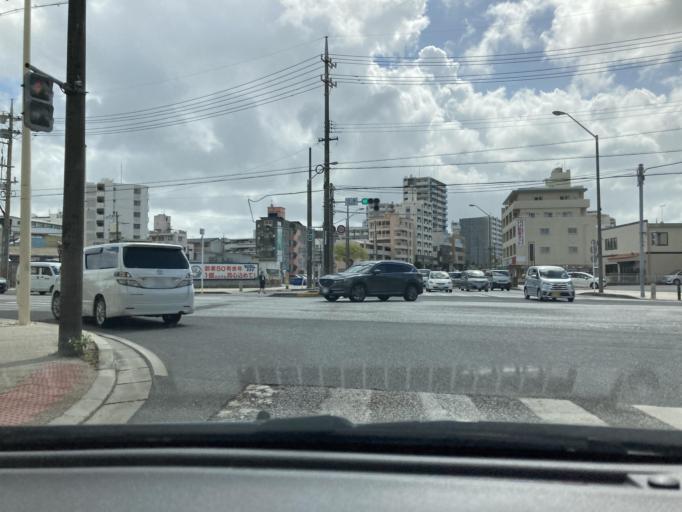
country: JP
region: Okinawa
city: Naha-shi
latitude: 26.2334
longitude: 127.7028
